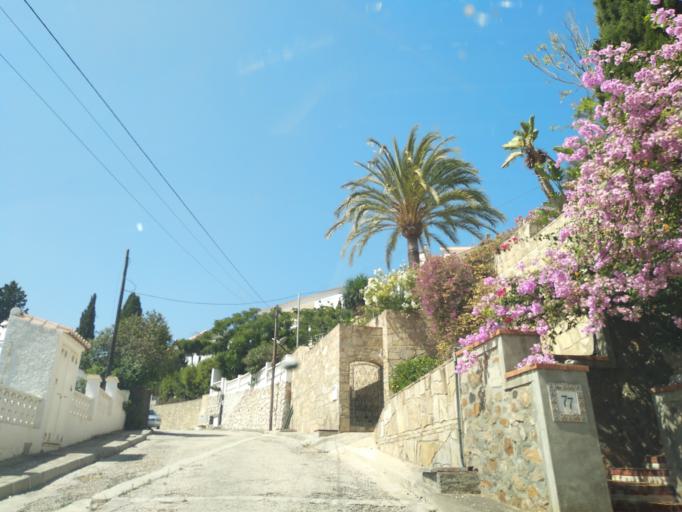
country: ES
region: Andalusia
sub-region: Provincia de Malaga
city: Iznate
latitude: 36.7203
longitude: -4.1882
